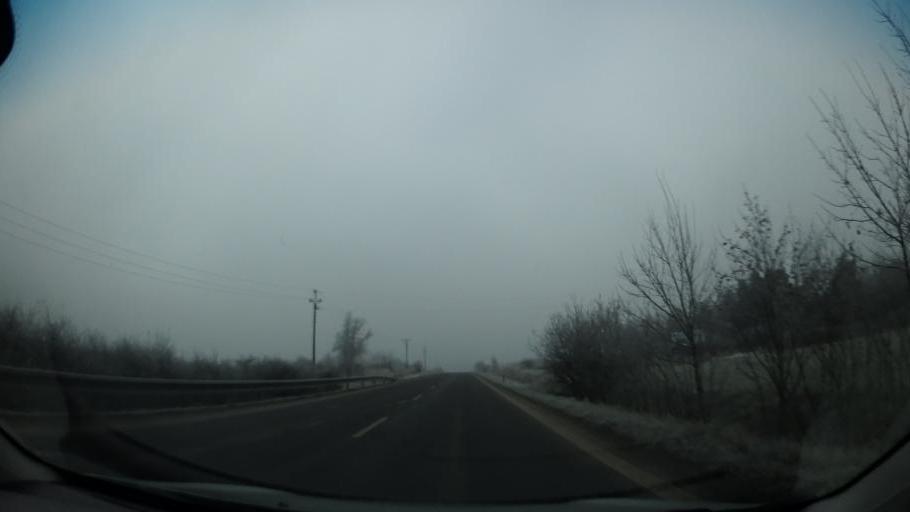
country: CZ
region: Vysocina
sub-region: Okres Trebic
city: Trebic
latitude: 49.2642
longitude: 15.9318
